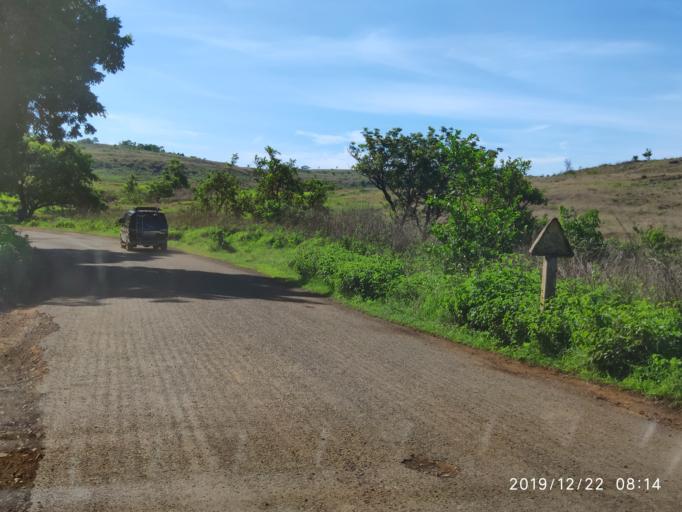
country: MG
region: Diana
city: Ambilobe
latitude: -12.9254
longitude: 49.1778
